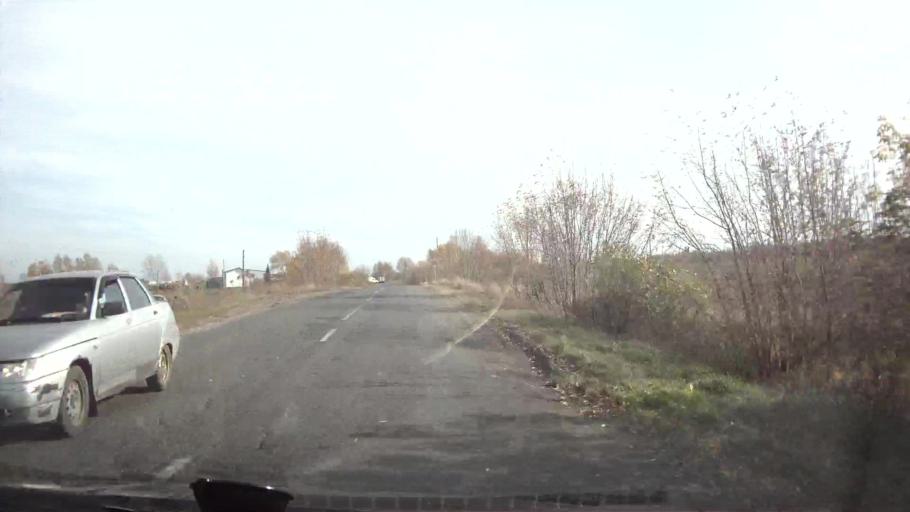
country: RU
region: Chuvashia
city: Alatyr'
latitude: 54.8438
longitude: 46.4701
